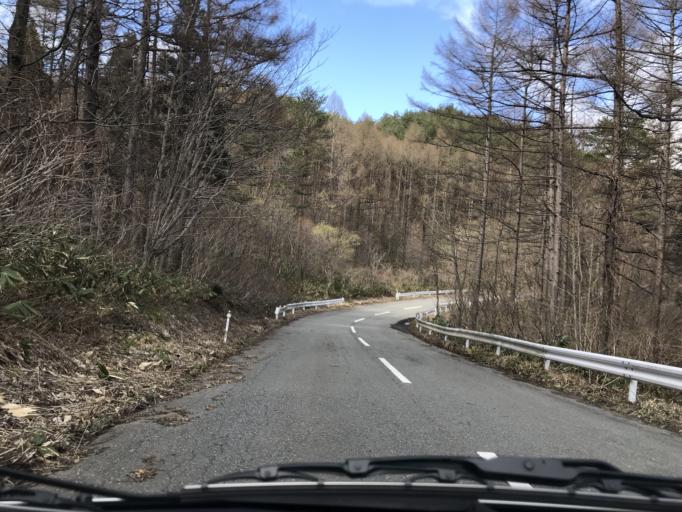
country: JP
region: Iwate
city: Mizusawa
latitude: 39.0634
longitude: 140.9719
